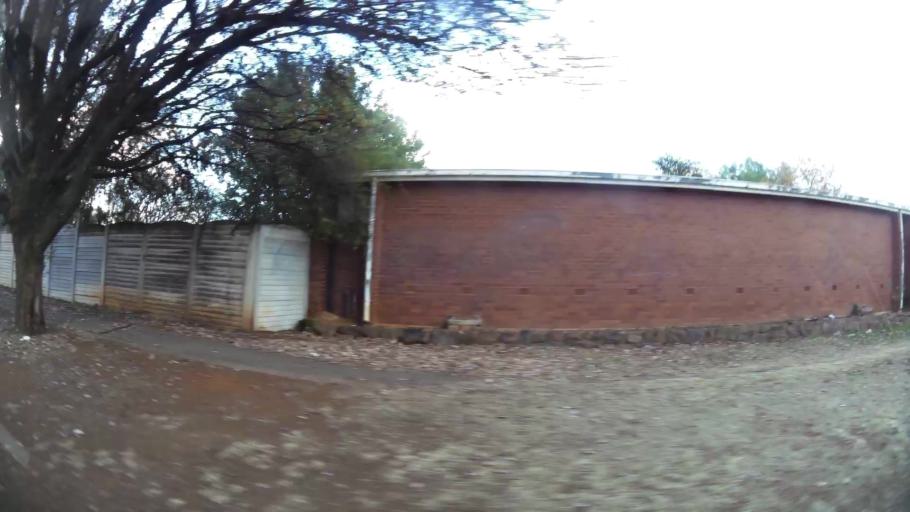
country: ZA
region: North-West
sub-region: Dr Kenneth Kaunda District Municipality
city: Potchefstroom
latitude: -26.7157
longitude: 27.0887
